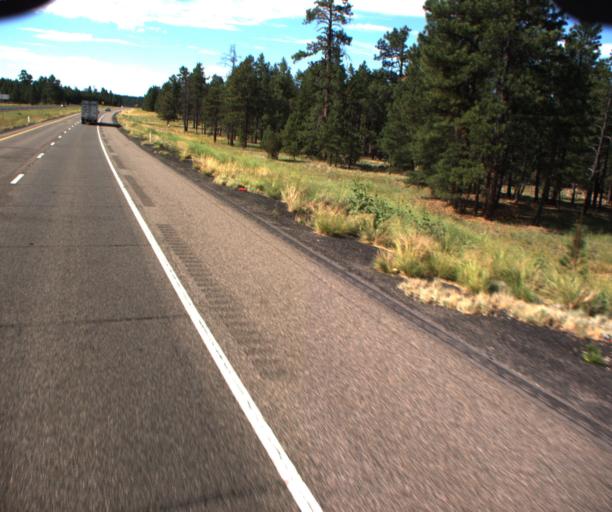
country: US
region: Arizona
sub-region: Coconino County
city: Sedona
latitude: 34.8983
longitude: -111.6416
